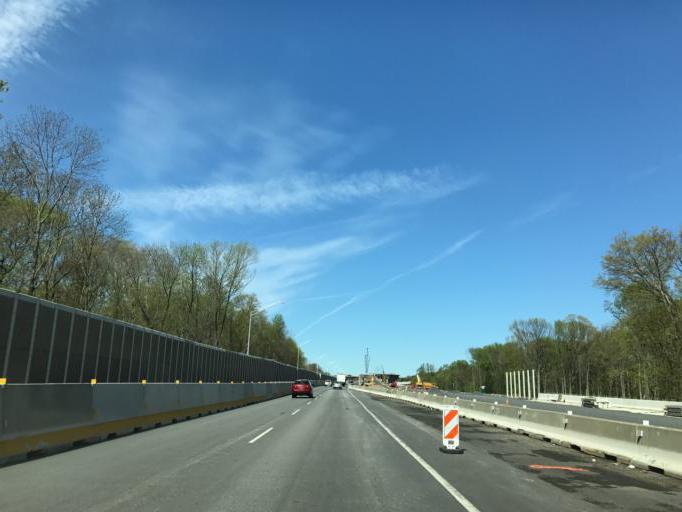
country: US
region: Pennsylvania
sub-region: Bucks County
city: Bristol
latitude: 40.1262
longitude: -74.8710
